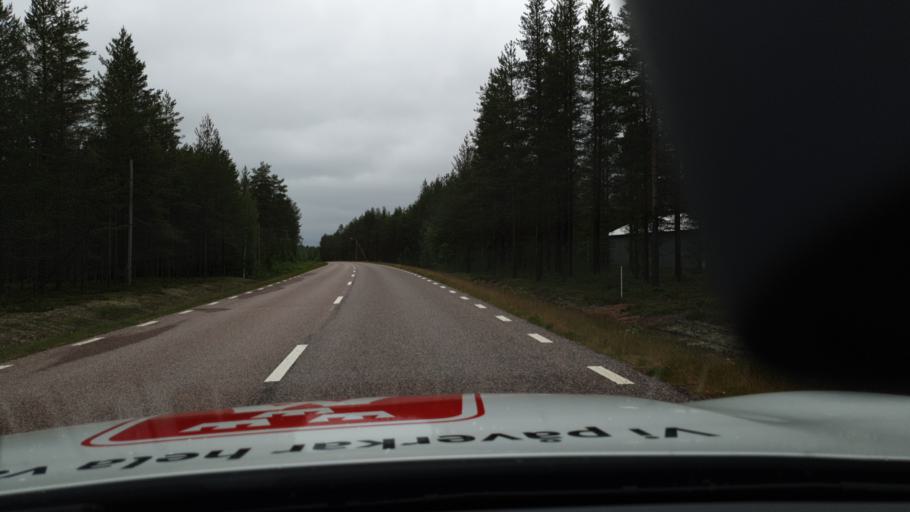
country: FI
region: Lapland
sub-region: Tunturi-Lappi
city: Kolari
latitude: 67.0209
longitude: 23.7274
